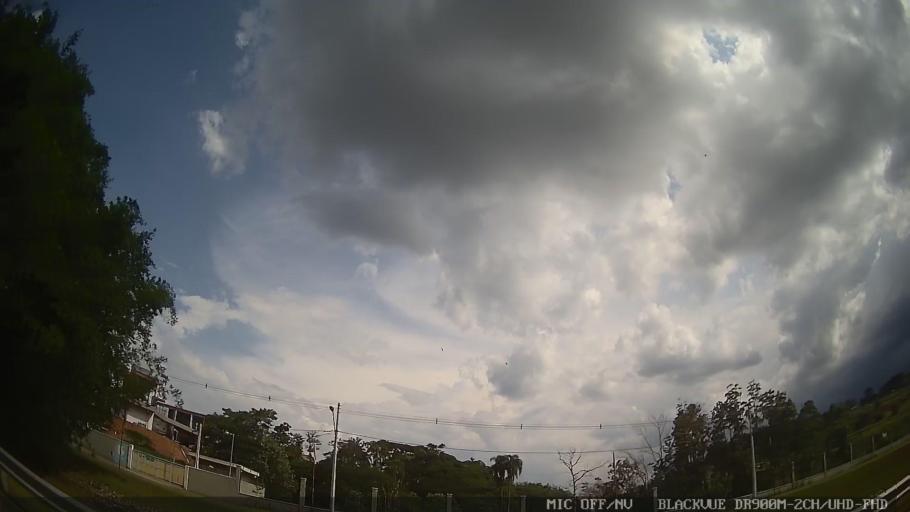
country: BR
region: Sao Paulo
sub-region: Itatiba
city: Itatiba
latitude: -23.0481
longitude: -46.8662
